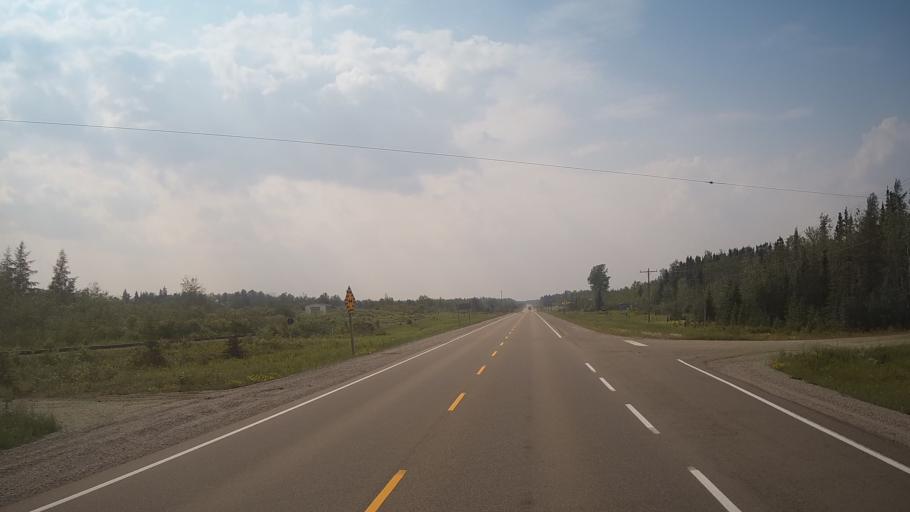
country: CA
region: Ontario
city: Kapuskasing
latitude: 49.4902
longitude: -82.7198
